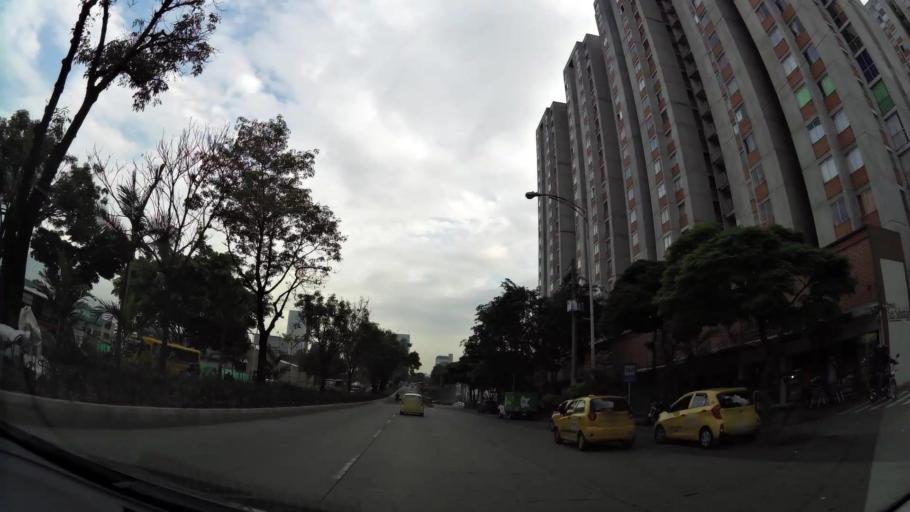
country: CO
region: Antioquia
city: Medellin
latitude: 6.2412
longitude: -75.5695
